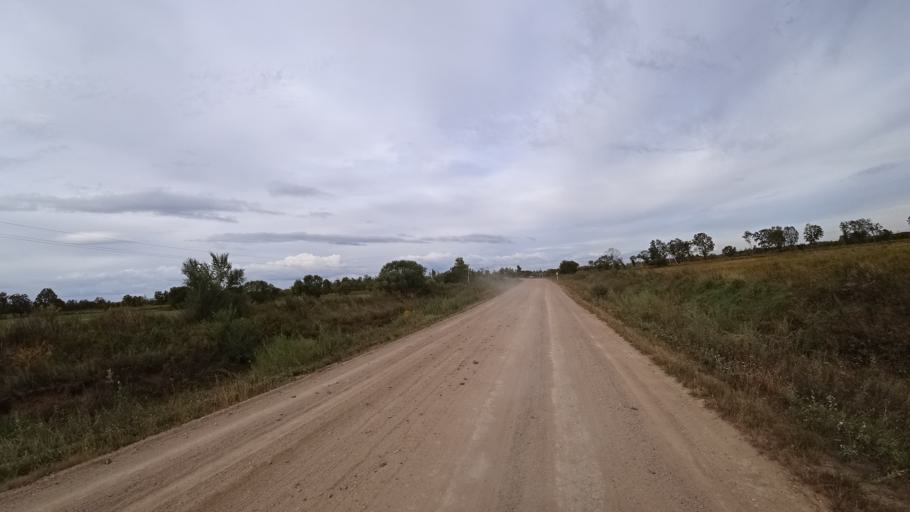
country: RU
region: Amur
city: Arkhara
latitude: 49.3522
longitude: 130.1335
